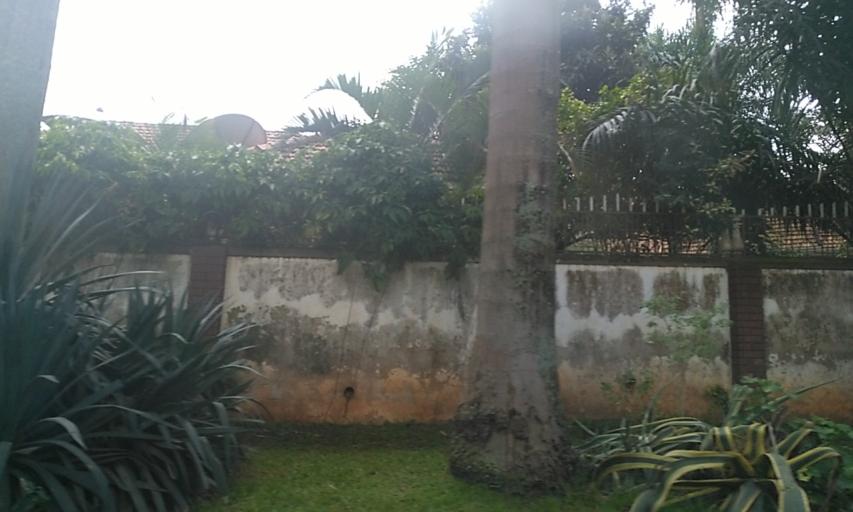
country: UG
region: Central Region
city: Kampala Central Division
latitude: 0.3400
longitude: 32.5892
